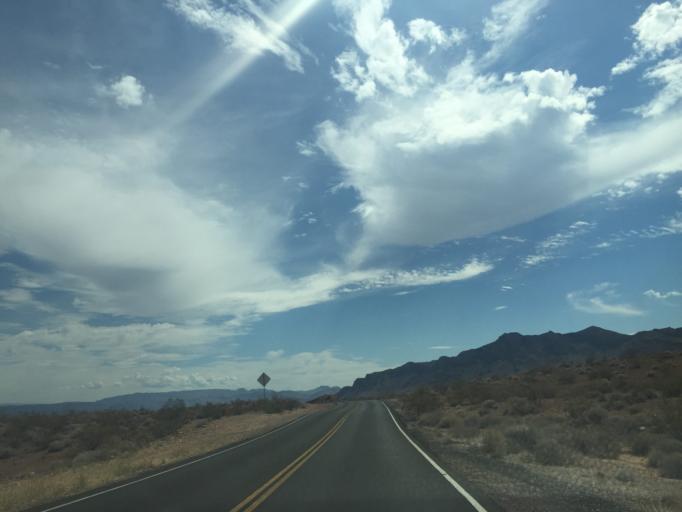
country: US
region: Nevada
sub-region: Clark County
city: Moapa Valley
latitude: 36.4250
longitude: -114.5279
